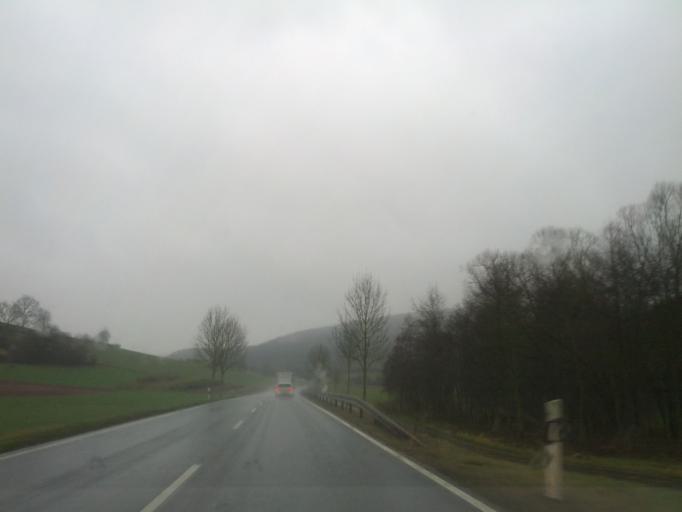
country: DE
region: Hesse
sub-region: Regierungsbezirk Kassel
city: Sontra
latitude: 51.0801
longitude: 9.9882
